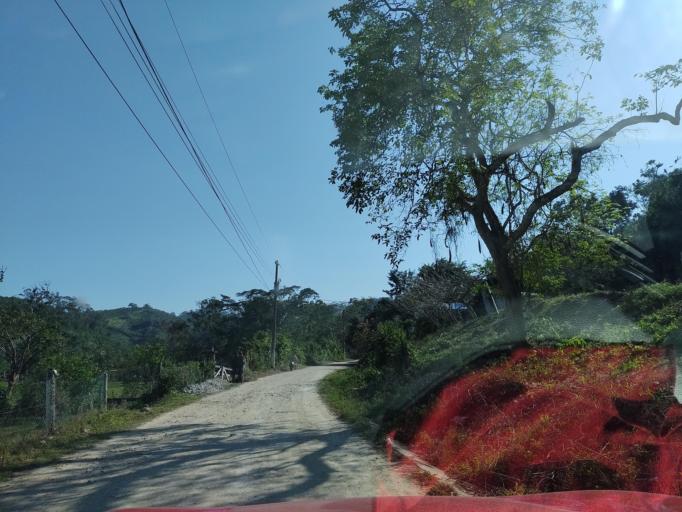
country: MX
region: Veracruz
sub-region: Papantla
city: Polutla
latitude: 20.4950
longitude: -97.1788
